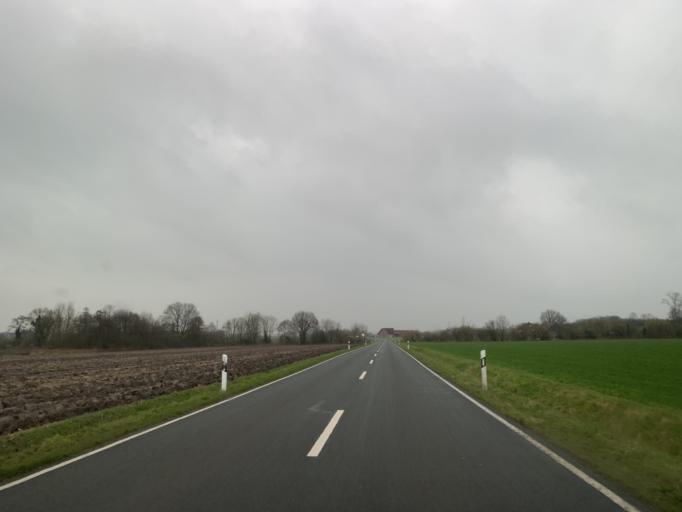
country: DE
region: North Rhine-Westphalia
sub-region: Regierungsbezirk Munster
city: Nottuln
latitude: 51.8609
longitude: 7.3506
